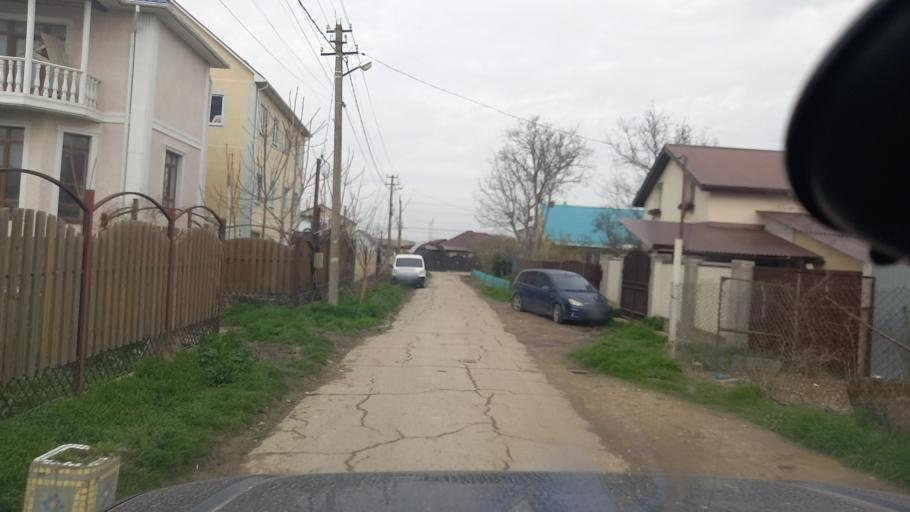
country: RU
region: Krasnodarskiy
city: Tsibanobalka
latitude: 44.9670
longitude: 37.3202
